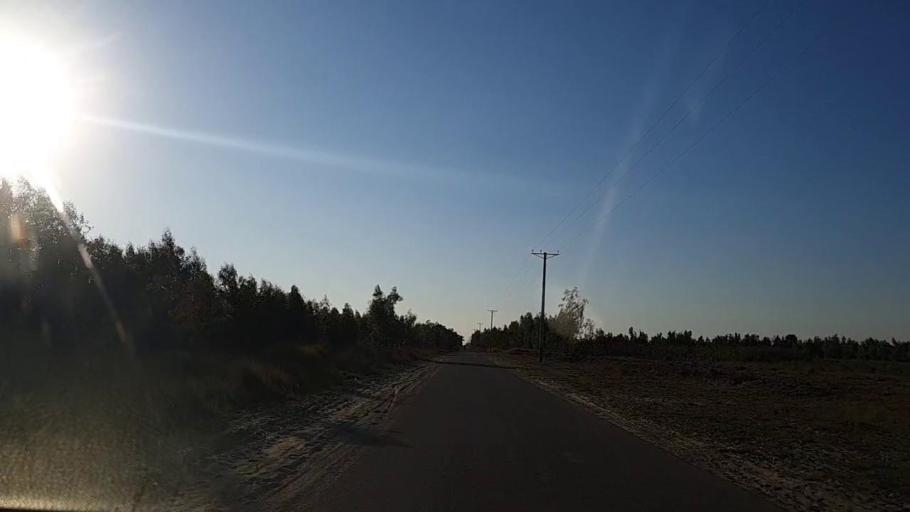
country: PK
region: Sindh
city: Khadro
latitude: 26.2790
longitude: 68.9024
